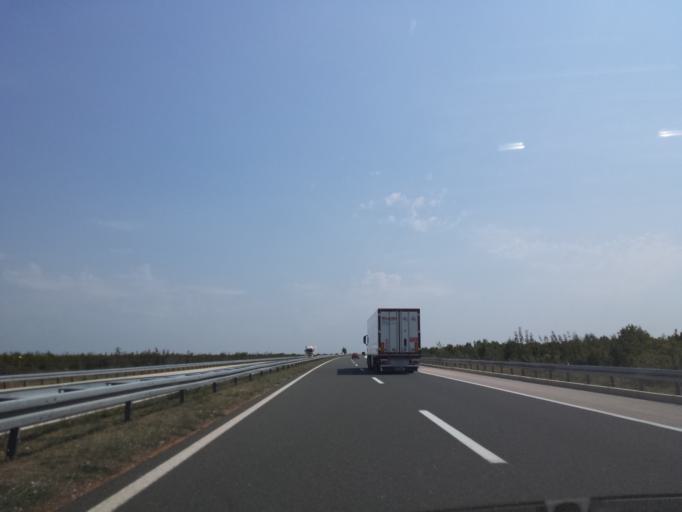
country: HR
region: Sibensko-Kniniska
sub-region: Grad Sibenik
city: Pirovac
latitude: 43.9219
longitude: 15.7349
